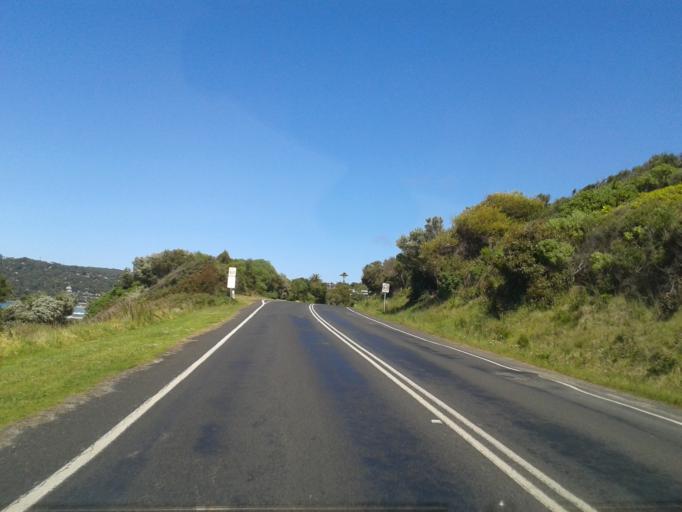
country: AU
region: Victoria
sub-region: Surf Coast
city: Anglesea
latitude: -38.5269
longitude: 143.9837
